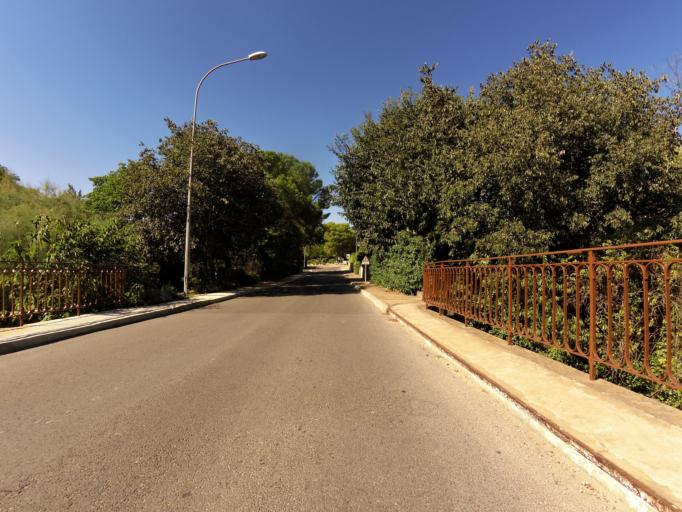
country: FR
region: Languedoc-Roussillon
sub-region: Departement du Gard
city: Vergeze
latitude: 43.7412
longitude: 4.2260
